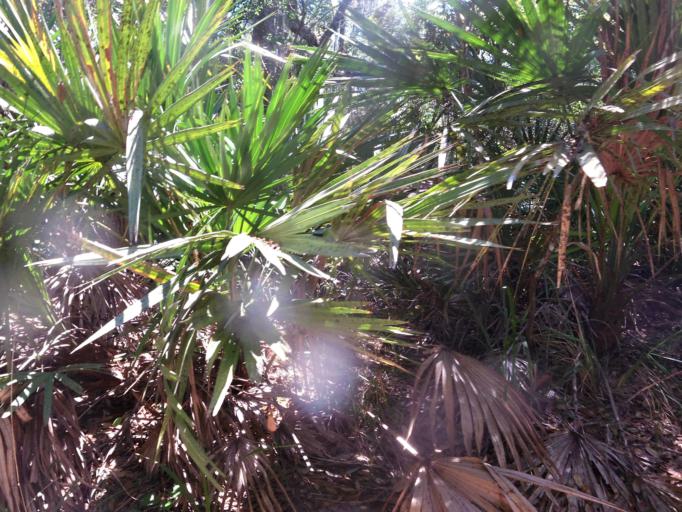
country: US
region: Florida
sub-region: Flagler County
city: Flagler Beach
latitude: 29.4118
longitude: -81.1292
